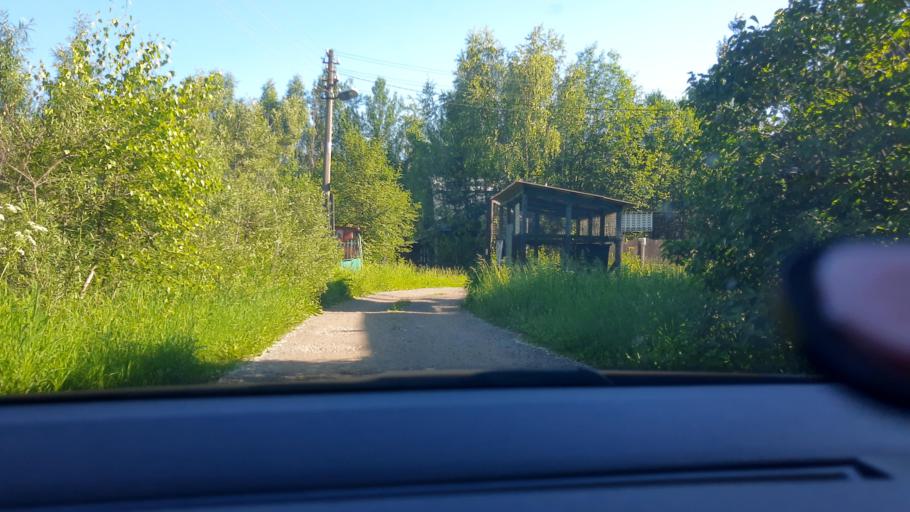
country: RU
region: Moskovskaya
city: Elektrogorsk
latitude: 55.8928
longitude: 38.7263
